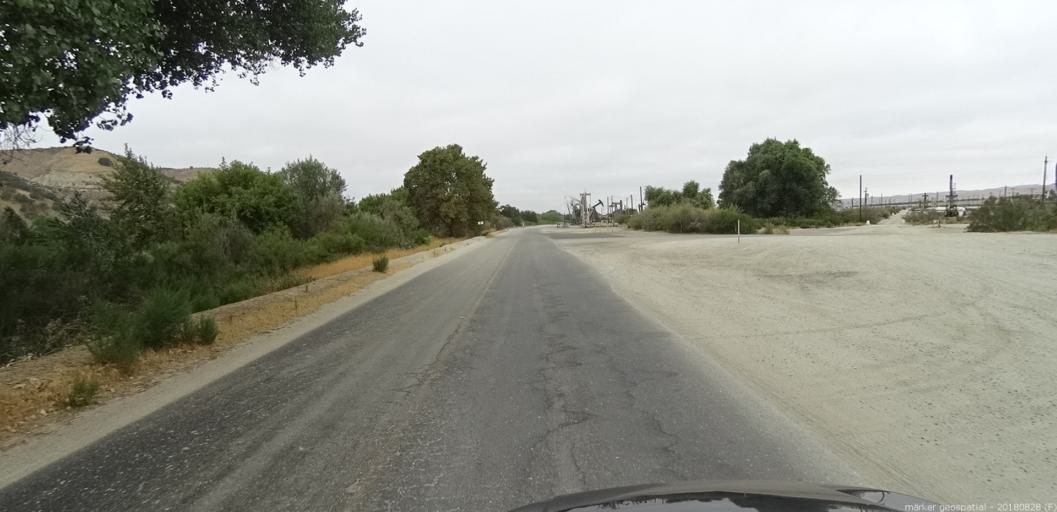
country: US
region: California
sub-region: San Luis Obispo County
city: Lake Nacimiento
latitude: 35.9582
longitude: -120.8780
